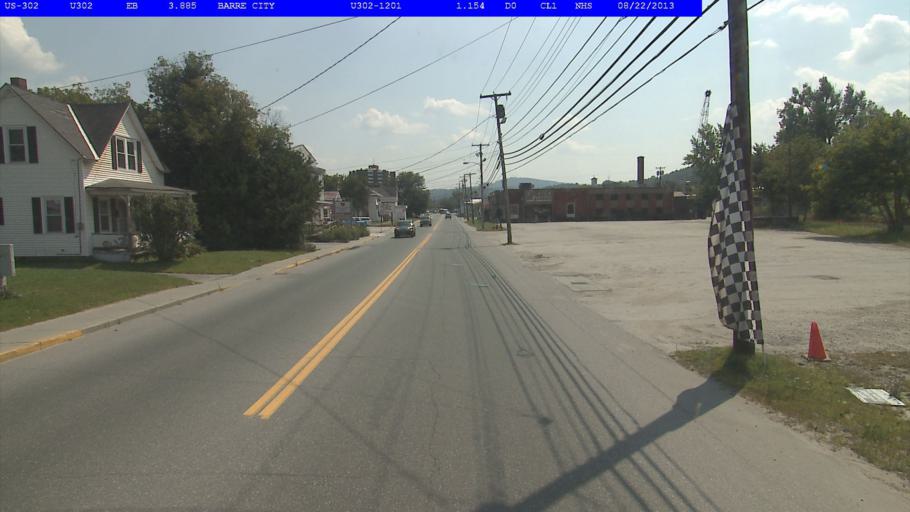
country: US
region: Vermont
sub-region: Washington County
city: Barre
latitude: 44.2089
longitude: -72.5145
